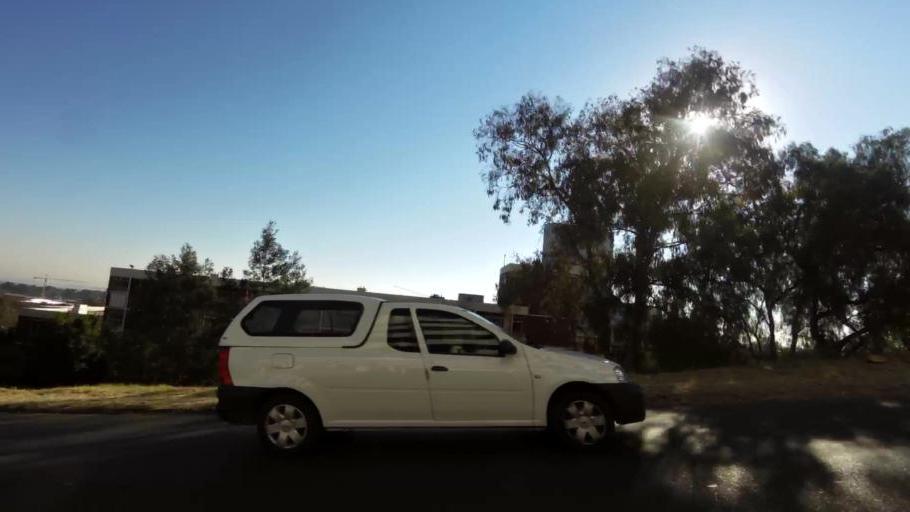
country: ZA
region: Gauteng
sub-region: City of Johannesburg Metropolitan Municipality
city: Johannesburg
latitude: -26.1900
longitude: 28.0083
